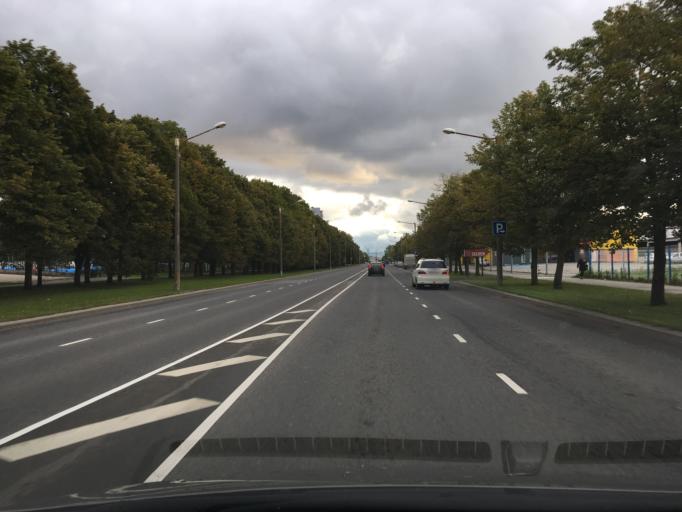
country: EE
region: Harju
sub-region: Tallinna linn
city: Kose
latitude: 59.4351
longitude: 24.8388
